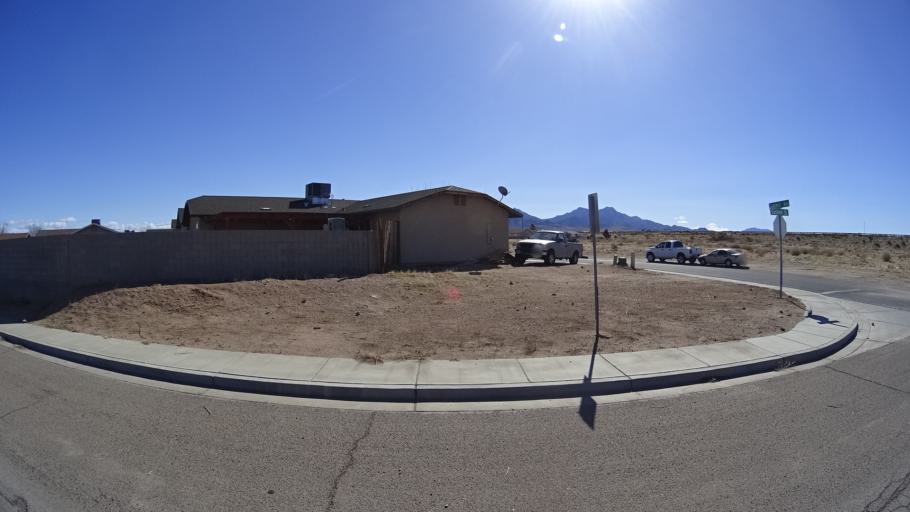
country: US
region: Arizona
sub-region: Mohave County
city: New Kingman-Butler
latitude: 35.2197
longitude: -114.0043
